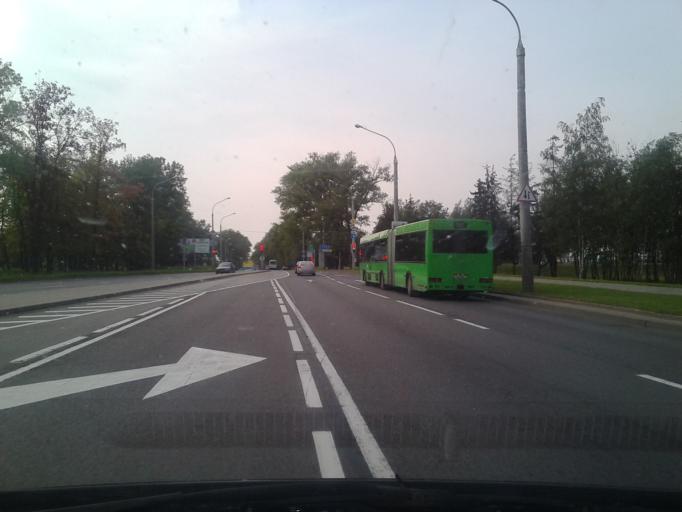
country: BY
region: Minsk
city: Minsk
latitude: 53.9225
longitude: 27.5105
